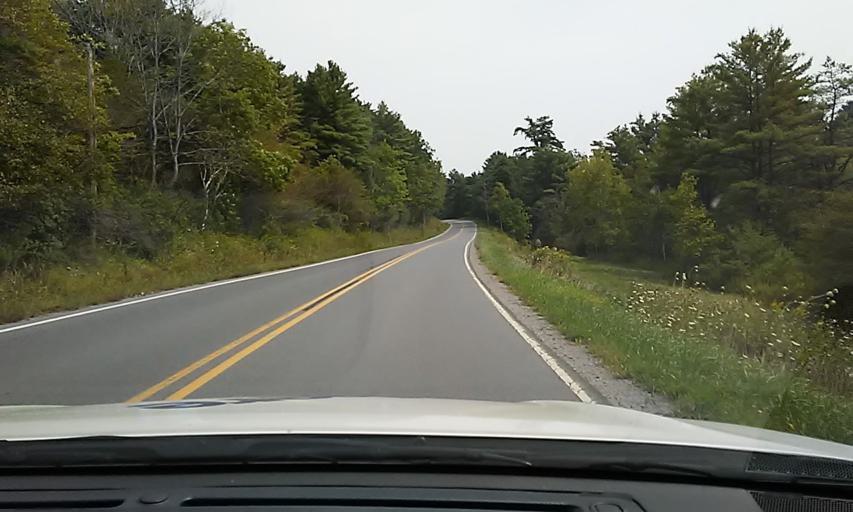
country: US
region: Pennsylvania
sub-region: Elk County
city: Ridgway
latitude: 41.2998
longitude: -78.6678
